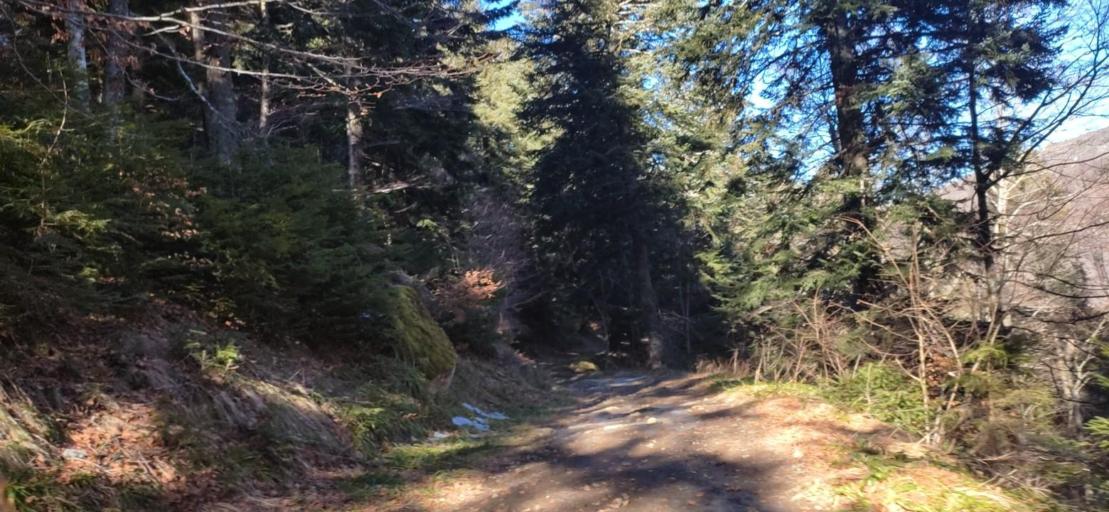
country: FR
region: Auvergne
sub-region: Departement du Puy-de-Dome
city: Mont-Dore
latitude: 45.5653
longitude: 2.8084
